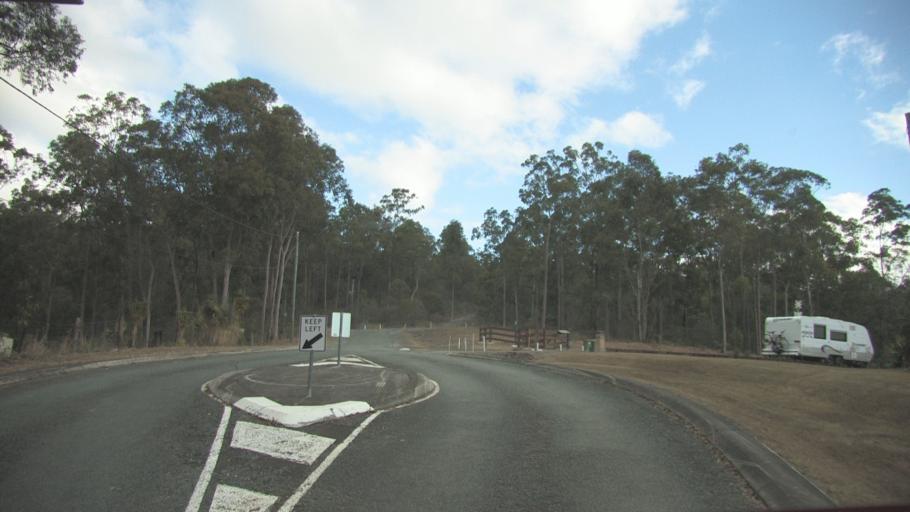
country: AU
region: Queensland
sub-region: Logan
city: Cedar Vale
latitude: -27.9338
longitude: 153.0526
